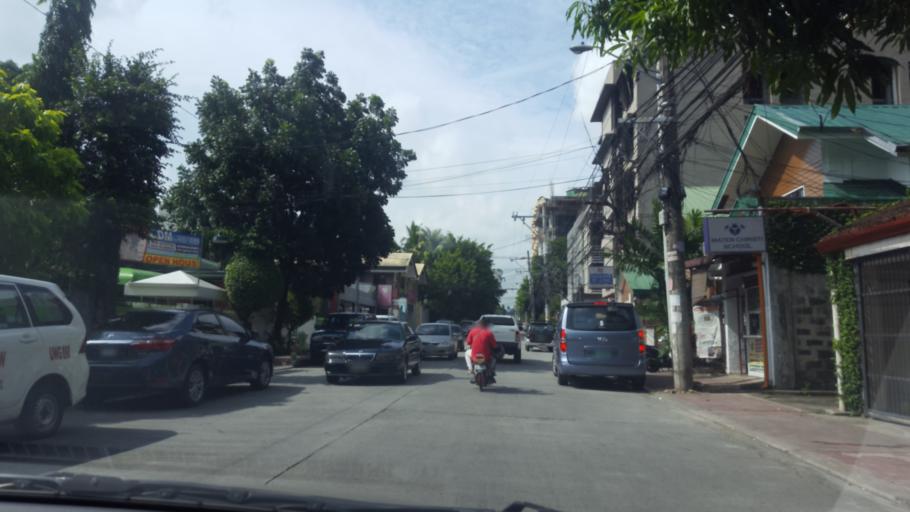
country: PH
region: Metro Manila
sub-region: Marikina
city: Calumpang
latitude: 14.6387
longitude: 121.0733
